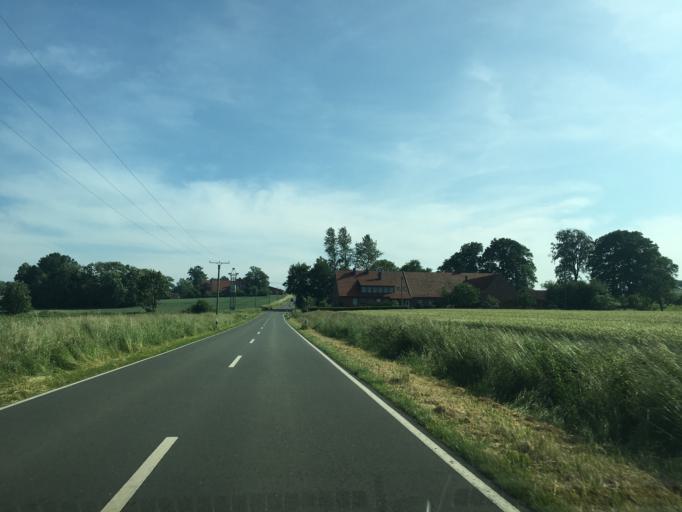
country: DE
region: North Rhine-Westphalia
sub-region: Regierungsbezirk Munster
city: Steinfurt
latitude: 52.1575
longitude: 7.3786
